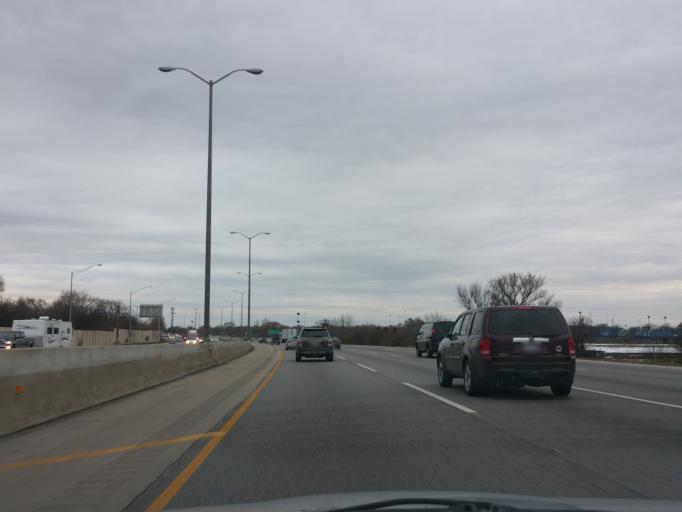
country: US
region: Illinois
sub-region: Cook County
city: Indian Head Park
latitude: 41.7698
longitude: -87.9061
